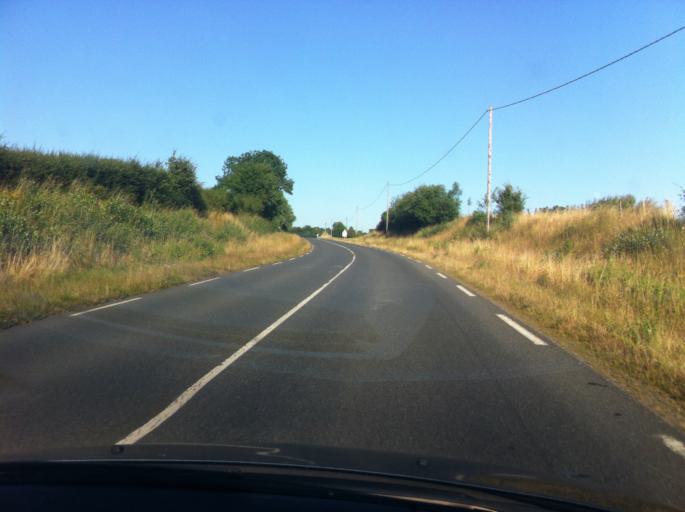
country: FR
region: Auvergne
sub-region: Departement de l'Allier
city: Chantelle
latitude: 46.3195
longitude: 3.1030
